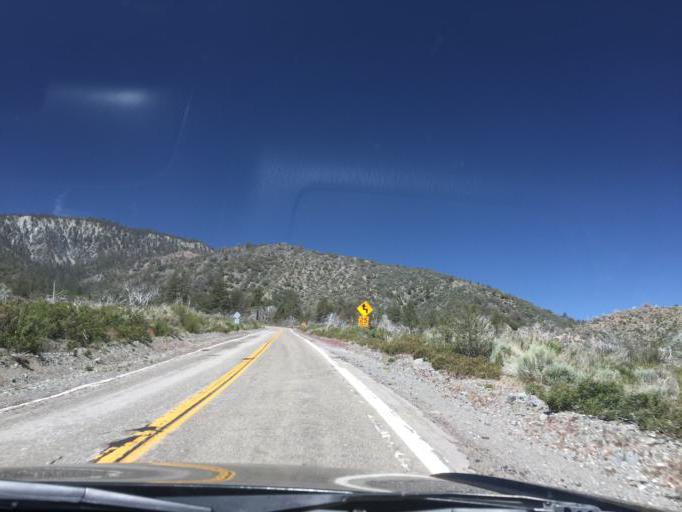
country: US
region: California
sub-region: San Bernardino County
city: Wrightwood
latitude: 34.3382
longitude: -117.5950
